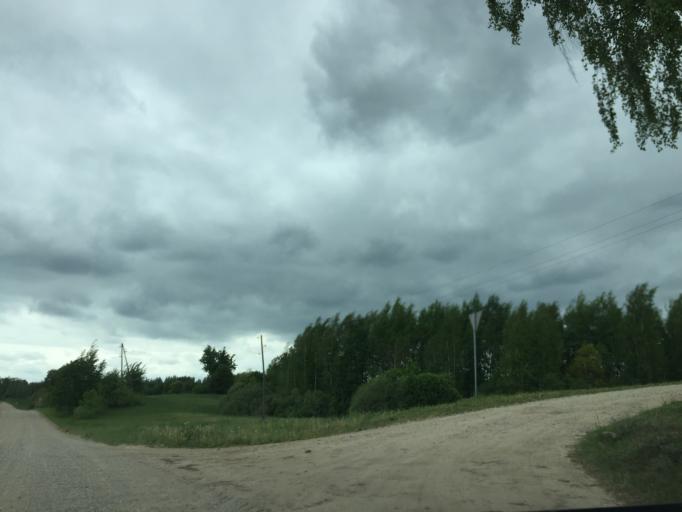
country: LV
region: Dagda
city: Dagda
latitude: 56.1874
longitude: 27.6414
